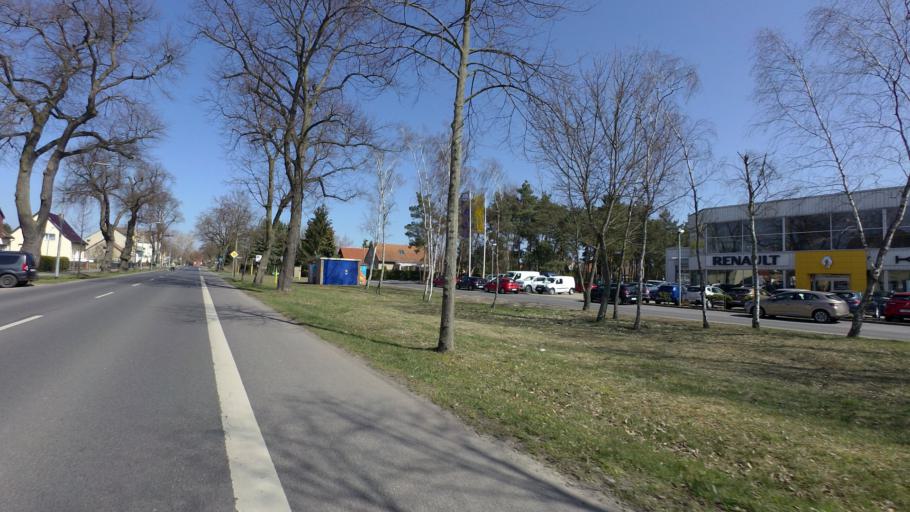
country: DE
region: Brandenburg
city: Oranienburg
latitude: 52.7699
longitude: 13.2467
